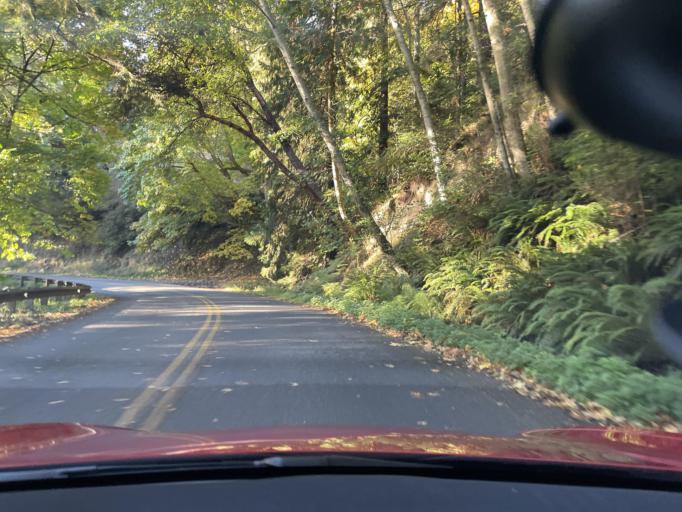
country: US
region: Washington
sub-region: San Juan County
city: Friday Harbor
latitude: 48.5137
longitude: -123.1431
